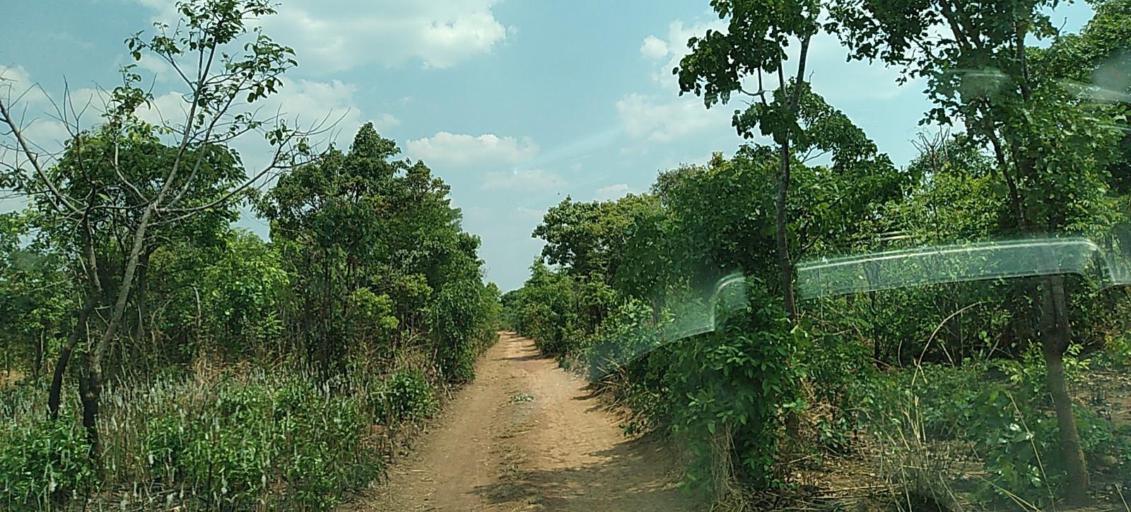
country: CD
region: Katanga
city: Kipushi
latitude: -12.0193
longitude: 27.4339
